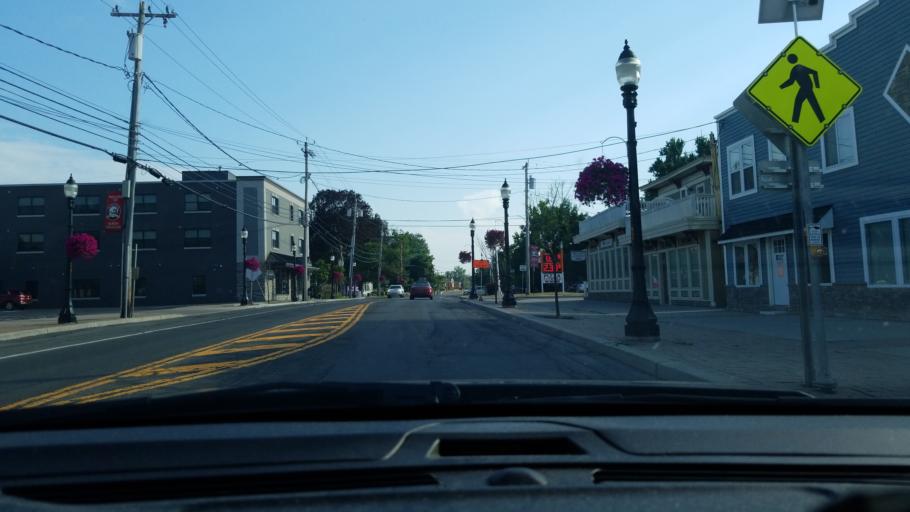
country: US
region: New York
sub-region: Onondaga County
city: North Syracuse
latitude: 43.1354
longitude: -76.1297
